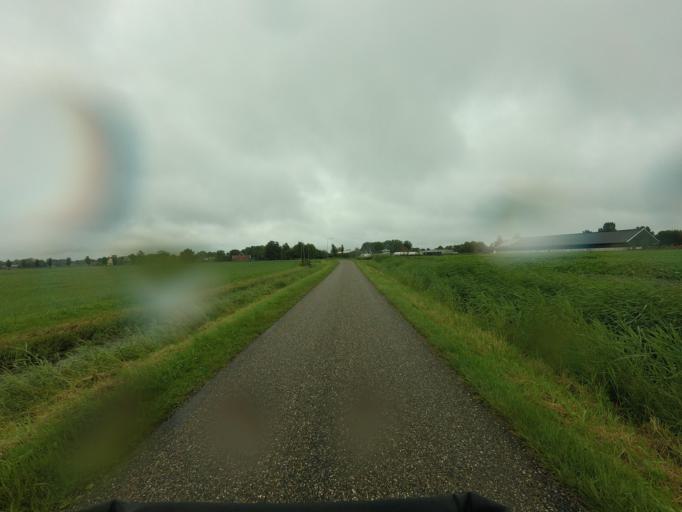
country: NL
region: North Holland
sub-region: Gemeente Opmeer
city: Opmeer
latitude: 52.7481
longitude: 4.9596
